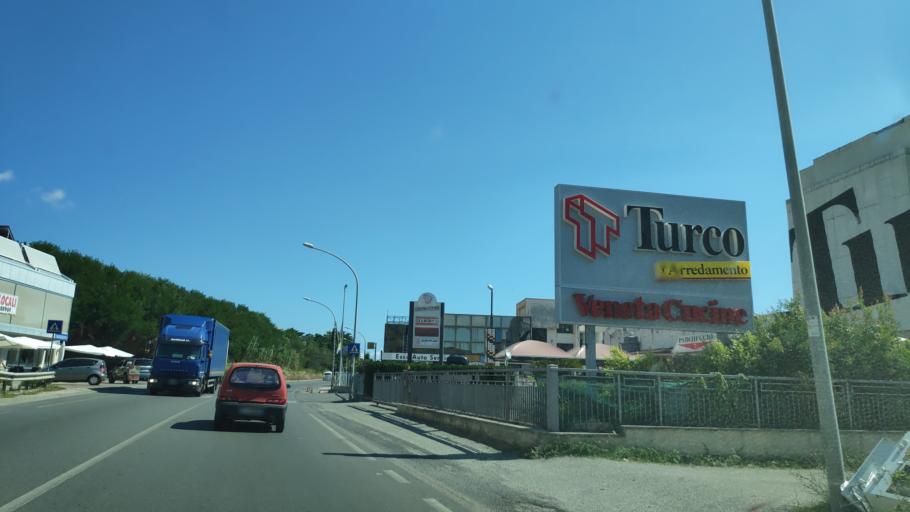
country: IT
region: Calabria
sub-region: Provincia di Cosenza
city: Campora San Giovanni
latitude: 39.0733
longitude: 16.0913
